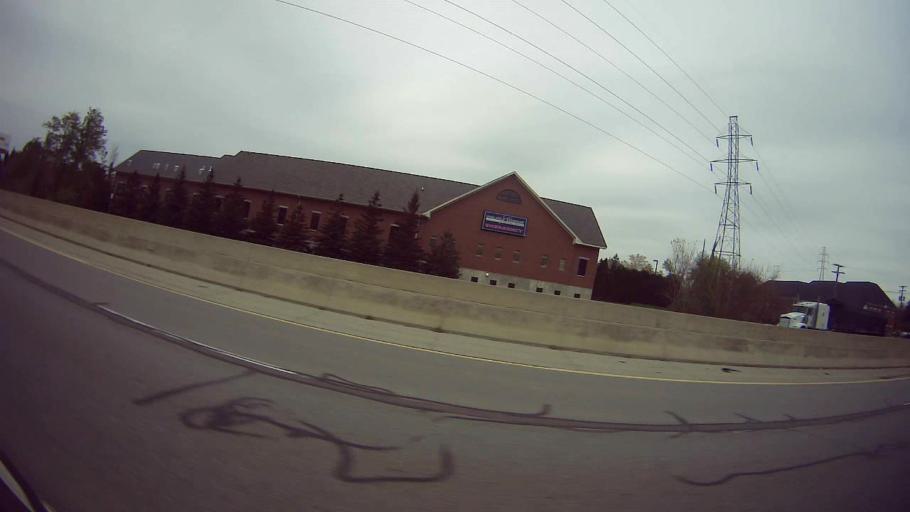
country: US
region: Michigan
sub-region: Oakland County
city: Sylvan Lake
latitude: 42.6178
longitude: -83.3193
